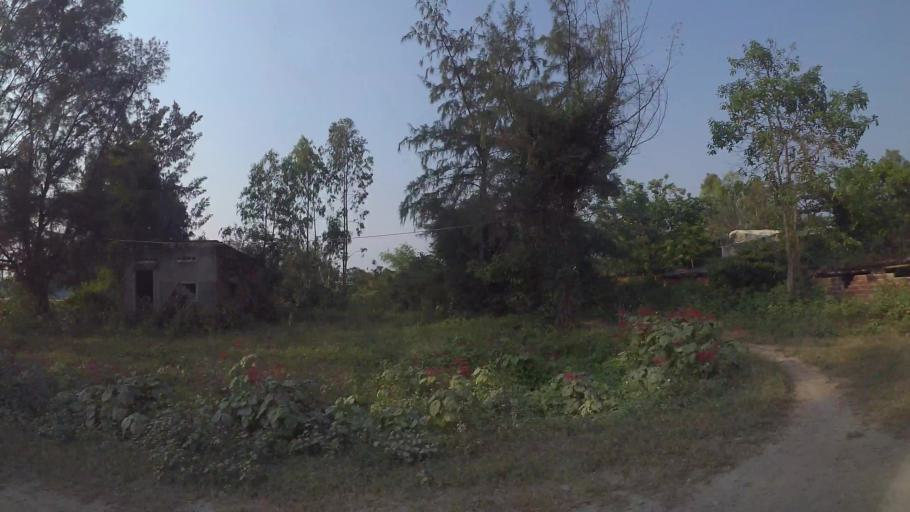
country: VN
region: Da Nang
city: Ngu Hanh Son
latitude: 15.9633
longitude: 108.2643
